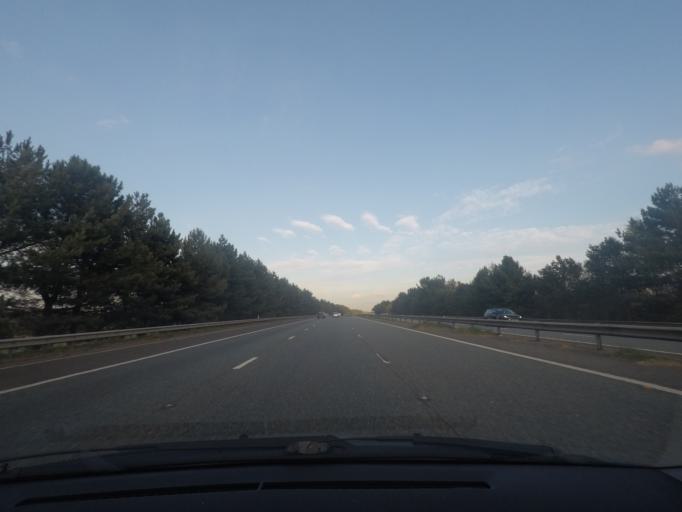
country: GB
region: England
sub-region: North Lincolnshire
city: Worlaby
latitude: 53.5769
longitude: -0.4591
